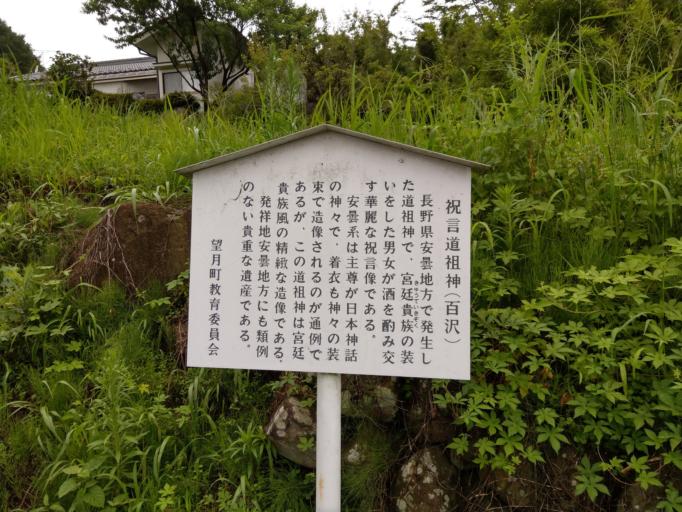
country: JP
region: Nagano
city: Komoro
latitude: 36.2694
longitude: 138.3780
